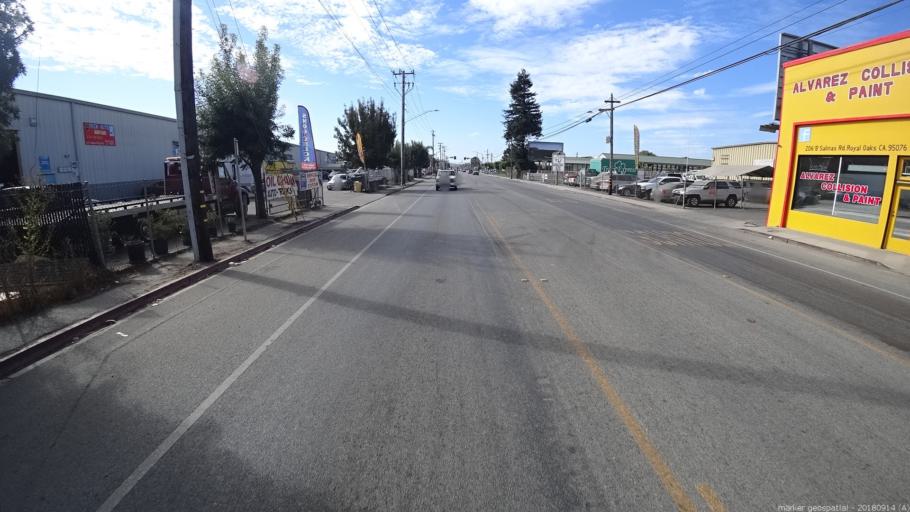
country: US
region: California
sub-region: Monterey County
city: Pajaro
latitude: 36.9004
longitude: -121.7481
